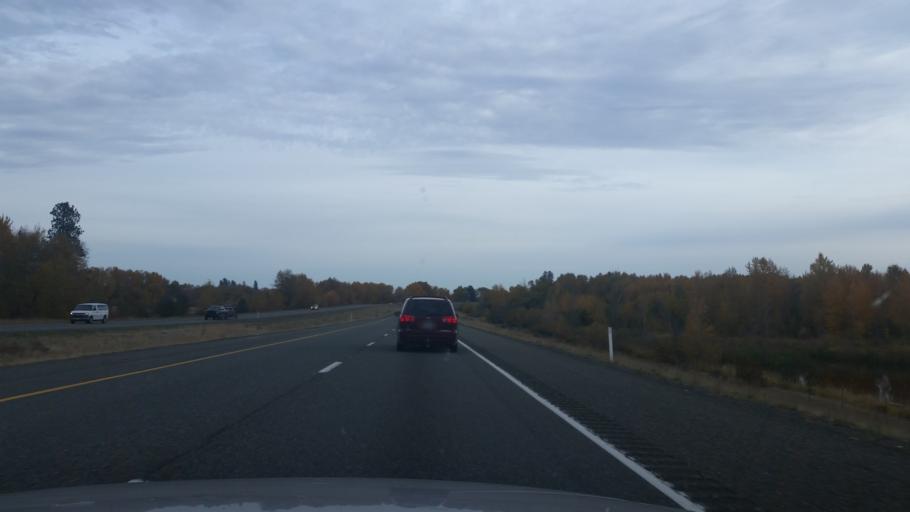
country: US
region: Washington
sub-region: Kittitas County
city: Ellensburg
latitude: 47.0430
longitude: -120.6367
